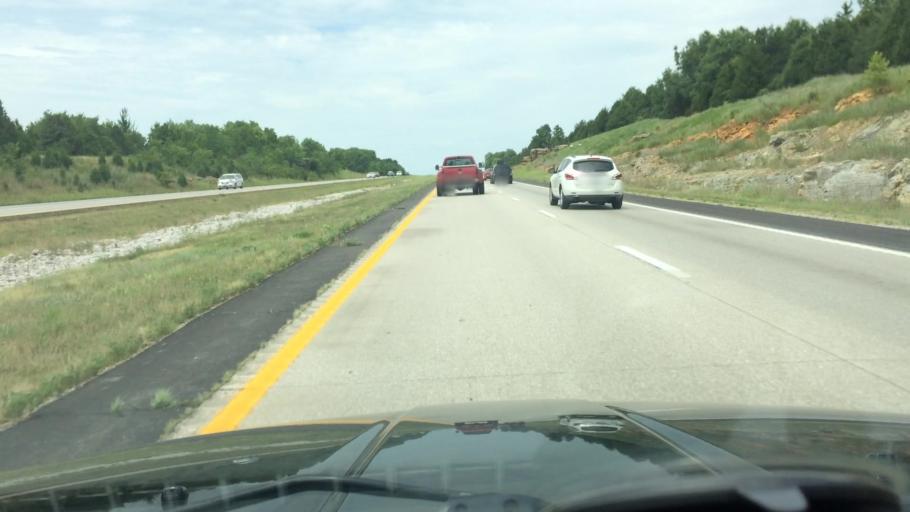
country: US
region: Missouri
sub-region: Greene County
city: Willard
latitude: 37.4393
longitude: -93.3555
